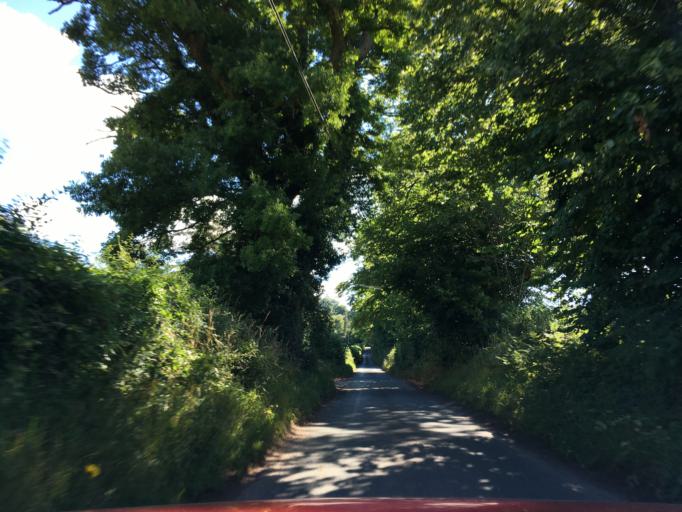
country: GB
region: England
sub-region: Herefordshire
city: Brockhampton
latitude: 51.9756
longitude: -2.5614
